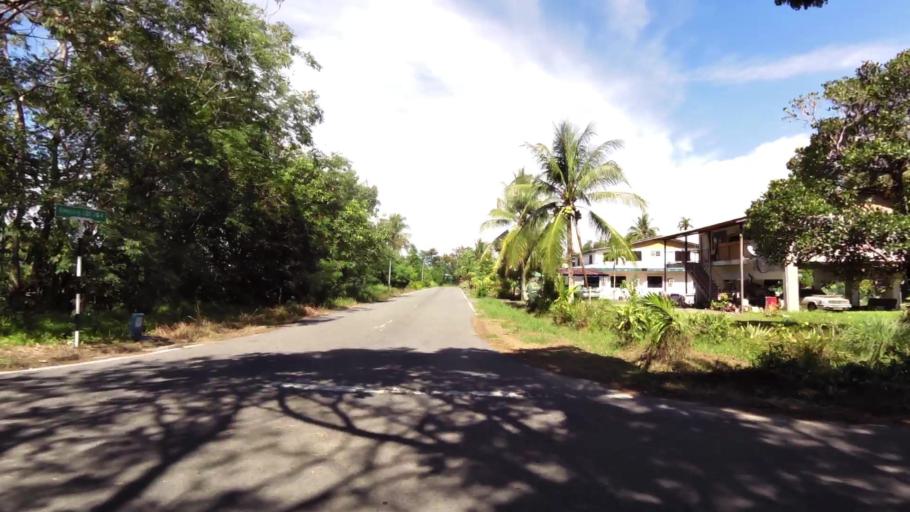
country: BN
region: Brunei and Muara
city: Bandar Seri Begawan
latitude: 5.0020
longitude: 115.0527
